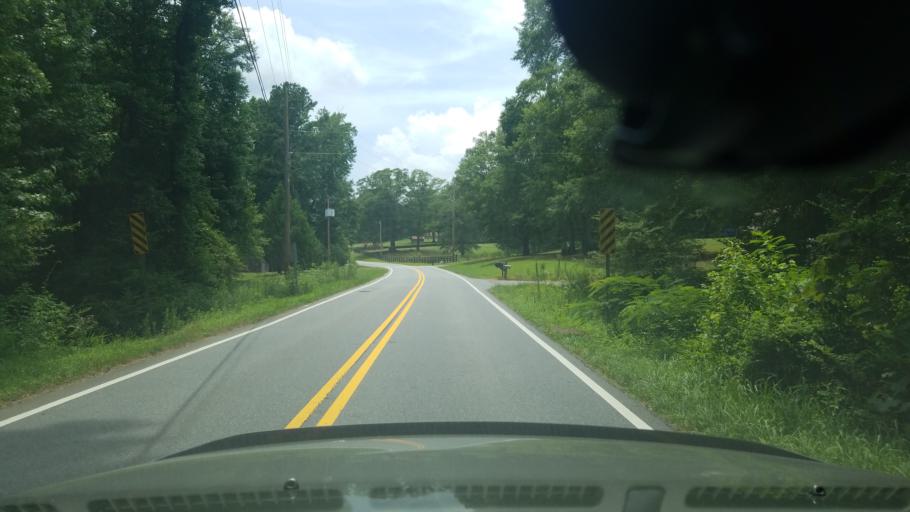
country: US
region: Georgia
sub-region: Forsyth County
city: Cumming
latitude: 34.1925
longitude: -84.2107
